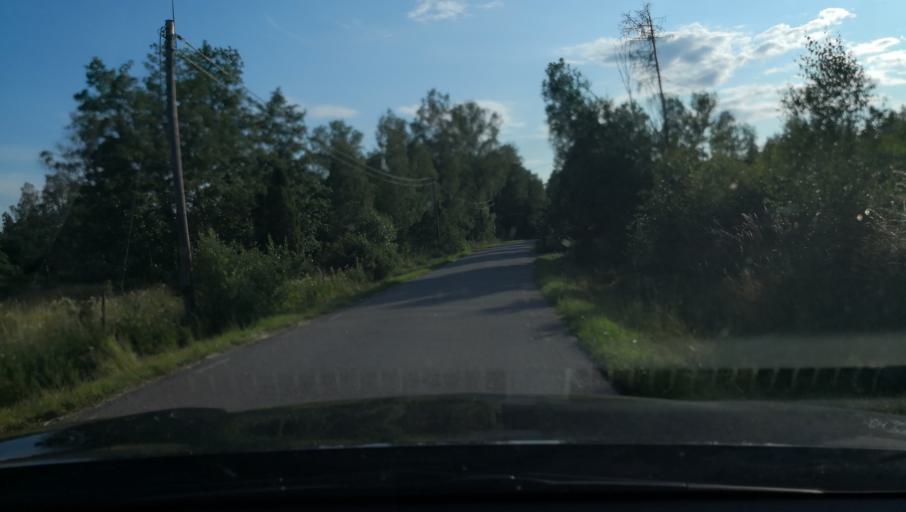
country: SE
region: Uppsala
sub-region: Osthammars Kommun
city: Osterbybruk
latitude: 60.0194
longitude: 17.9463
